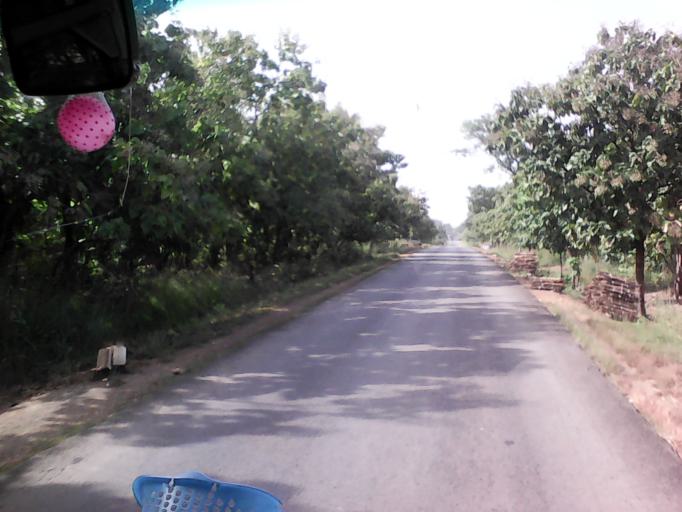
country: TG
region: Centrale
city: Sokode
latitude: 9.1454
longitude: 1.1566
